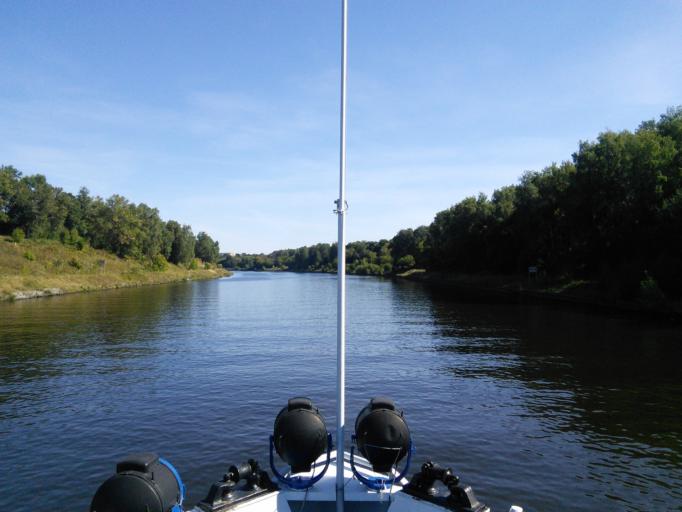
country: RU
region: Moskovskaya
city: Levoberezhnaya
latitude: 55.9112
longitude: 37.4783
